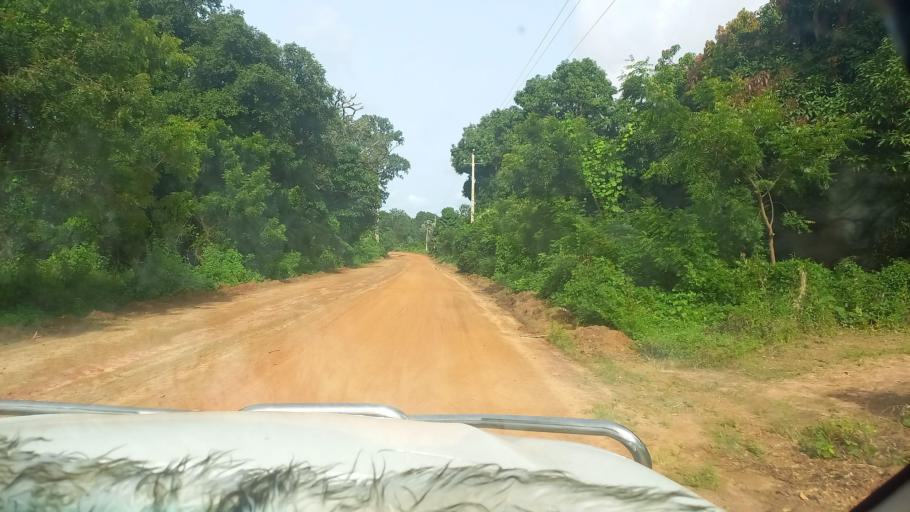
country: SN
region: Ziguinchor
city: Ziguinchor
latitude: 12.6689
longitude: -16.2689
